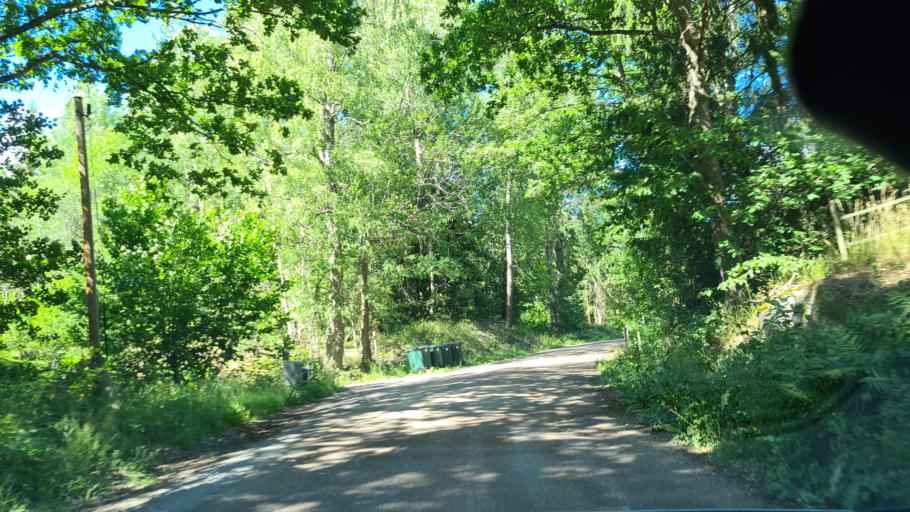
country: SE
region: OEstergoetland
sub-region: Norrkopings Kommun
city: Krokek
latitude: 58.6738
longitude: 16.4225
